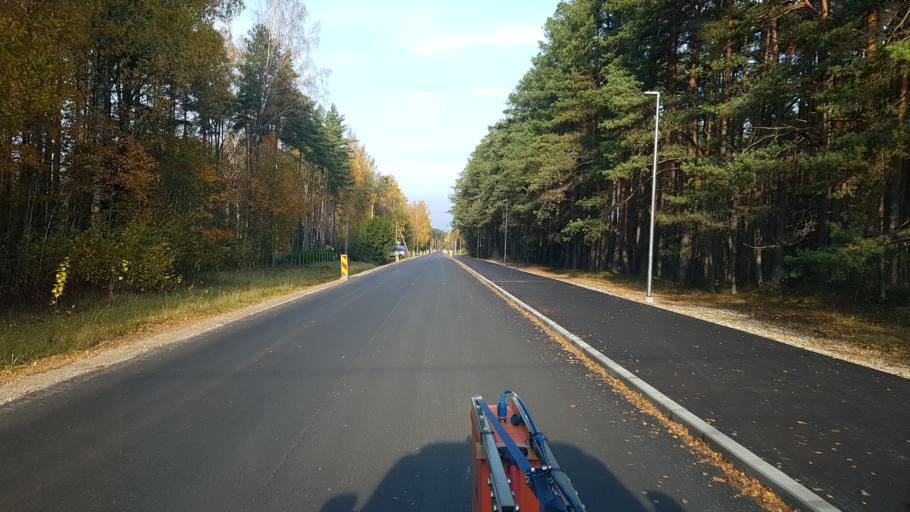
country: EE
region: Paernumaa
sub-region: Paikuse vald
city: Paikuse
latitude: 58.3561
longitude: 24.6157
